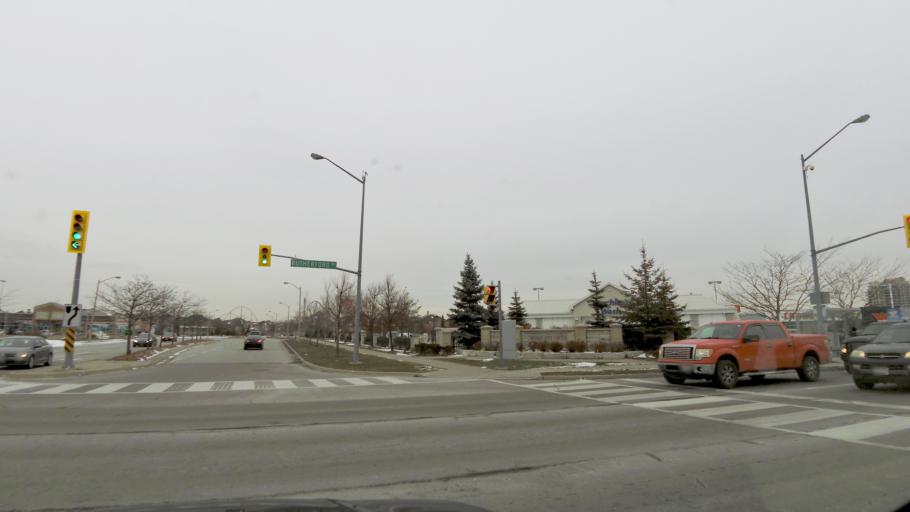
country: CA
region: Ontario
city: Vaughan
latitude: 43.8292
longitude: -79.5391
